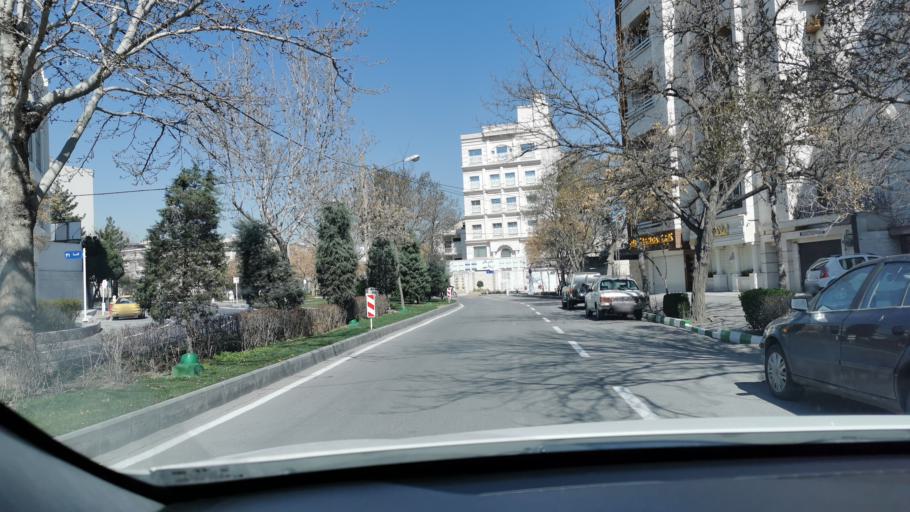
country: IR
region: Razavi Khorasan
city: Mashhad
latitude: 36.2884
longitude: 59.5733
